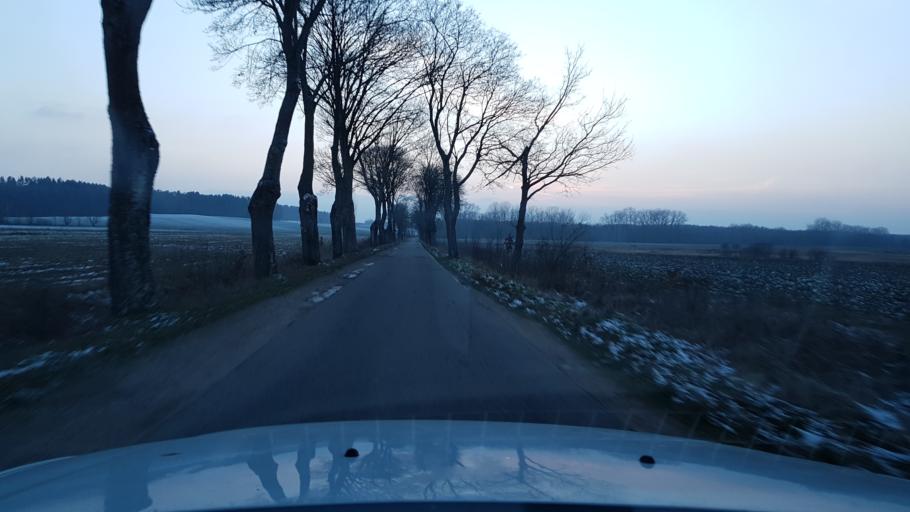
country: PL
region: West Pomeranian Voivodeship
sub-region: Powiat bialogardzki
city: Karlino
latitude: 53.9957
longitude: 15.8256
